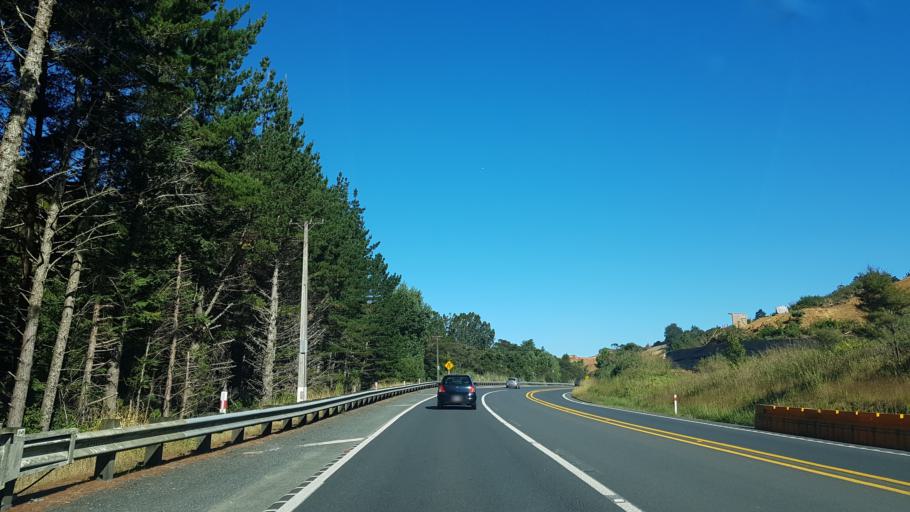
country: NZ
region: Auckland
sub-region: Auckland
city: Warkworth
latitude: -36.4969
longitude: 174.6619
